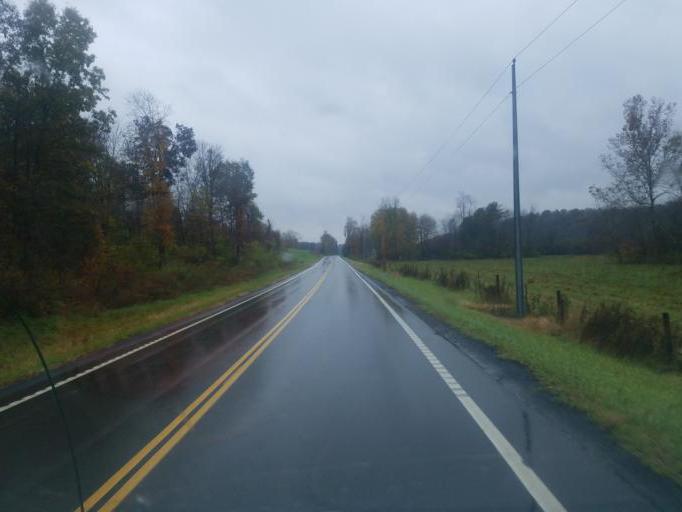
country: US
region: Ohio
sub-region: Muskingum County
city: Frazeysburg
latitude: 40.1758
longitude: -82.2284
